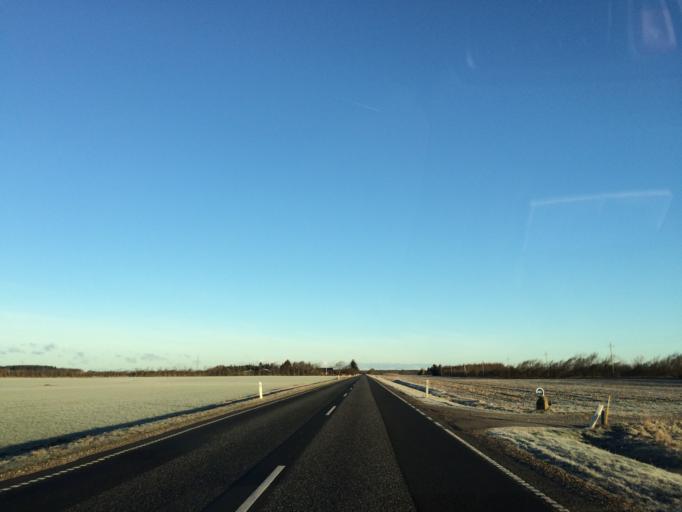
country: DK
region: Central Jutland
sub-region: Lemvig Kommune
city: Lemvig
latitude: 56.4398
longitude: 8.2966
